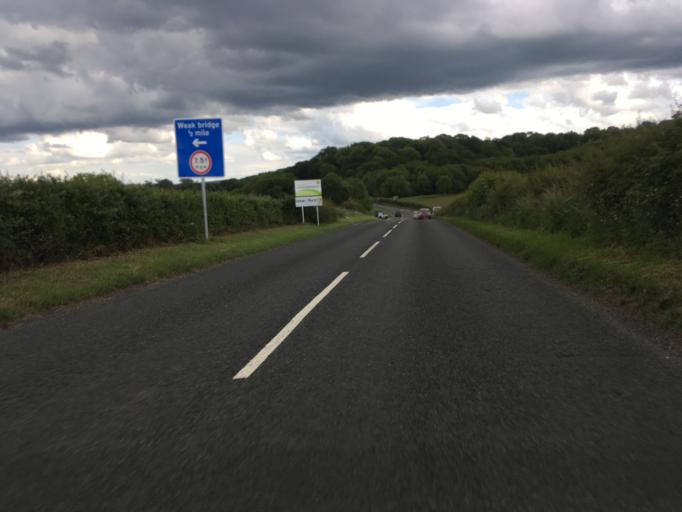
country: GB
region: England
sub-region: Central Bedfordshire
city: Leighton Buzzard
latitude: 51.9302
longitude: -0.6857
